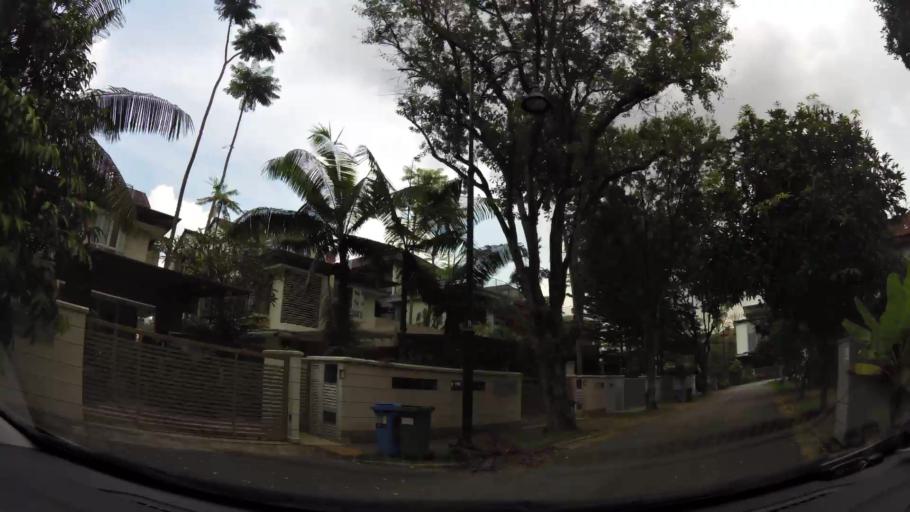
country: SG
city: Singapore
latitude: 1.3475
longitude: 103.8615
